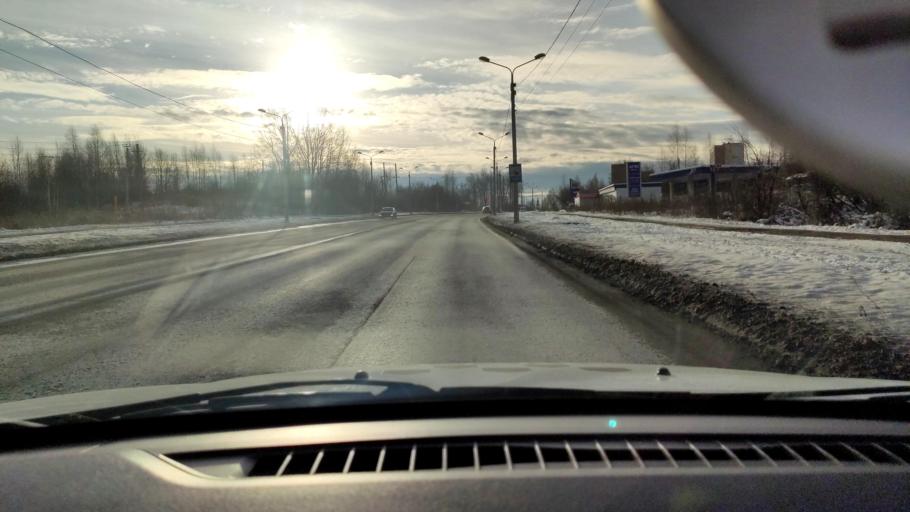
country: RU
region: Perm
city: Perm
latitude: 58.0680
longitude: 56.3662
